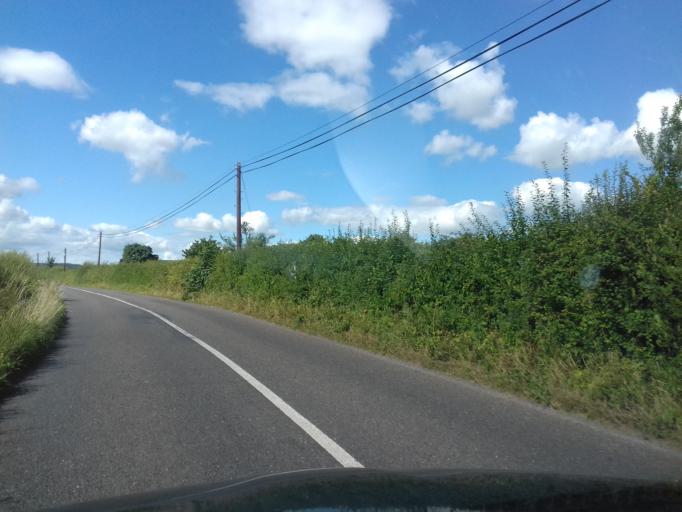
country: IE
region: Munster
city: Carrick-on-Suir
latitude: 52.3612
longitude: -7.4316
